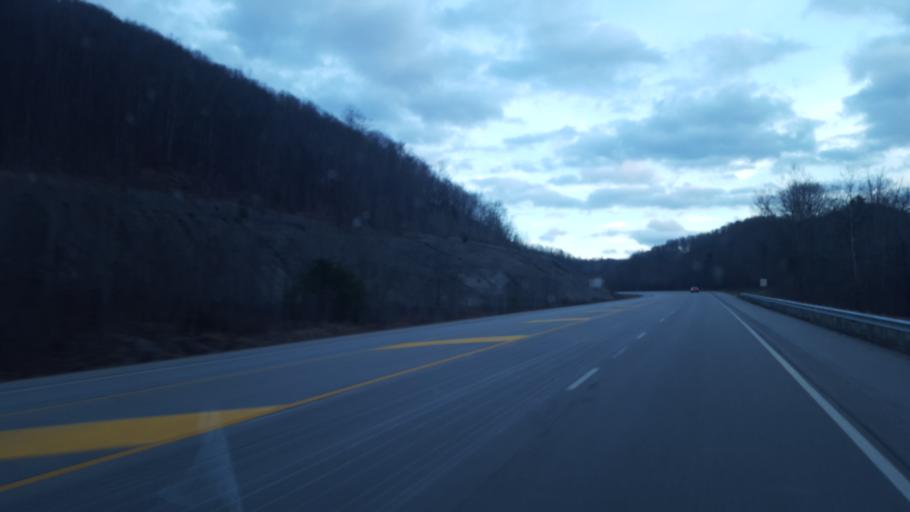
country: US
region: Kentucky
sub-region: Lewis County
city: Vanceburg
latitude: 38.5837
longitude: -83.3268
